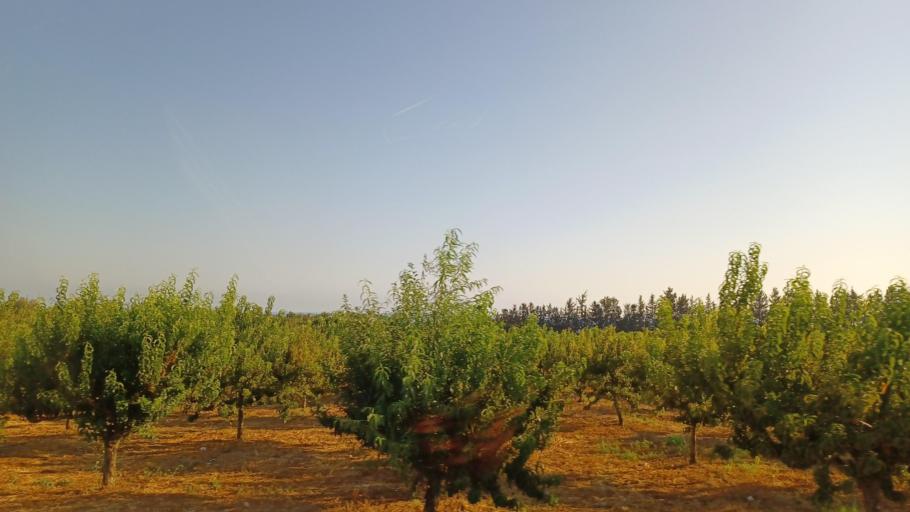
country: CY
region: Pafos
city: Polis
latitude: 35.0243
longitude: 32.3906
